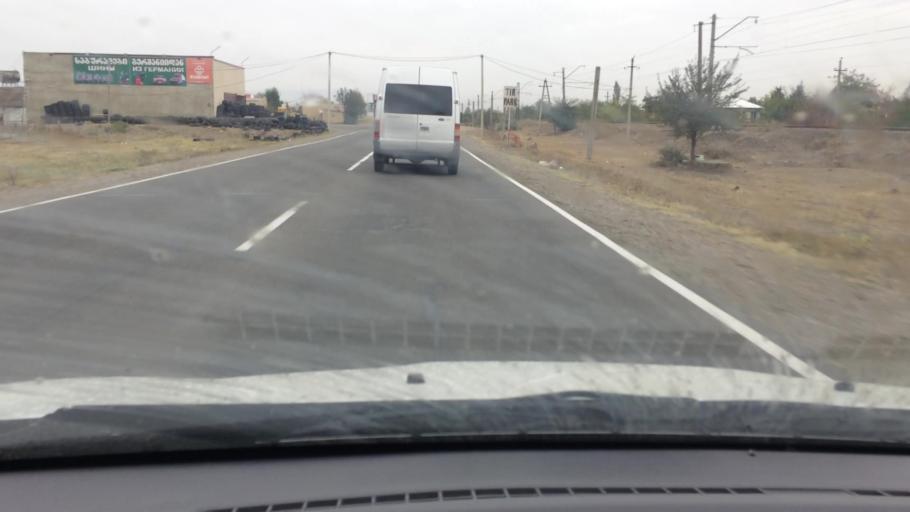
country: GE
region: Kvemo Kartli
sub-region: Marneuli
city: Marneuli
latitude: 41.4360
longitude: 44.8192
